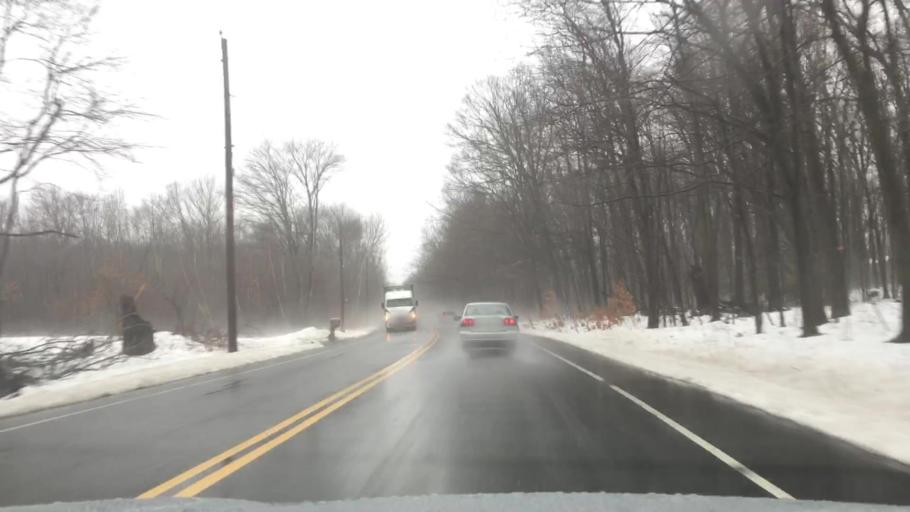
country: US
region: Massachusetts
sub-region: Hampden County
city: Ludlow
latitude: 42.2064
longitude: -72.4924
